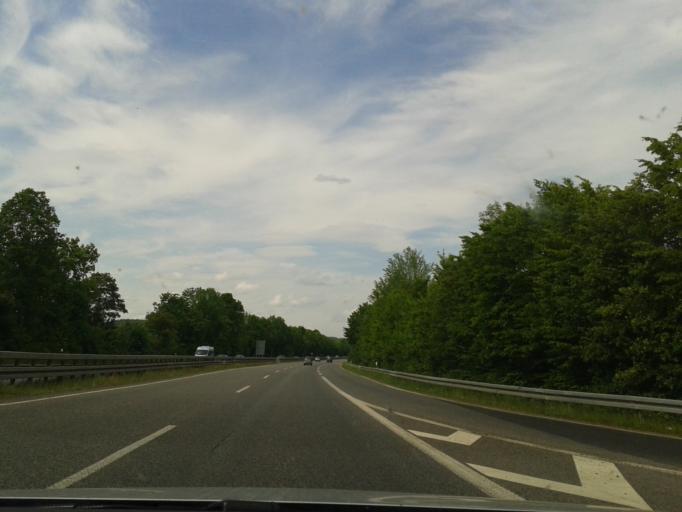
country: DE
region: Hesse
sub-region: Regierungsbezirk Giessen
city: Marburg an der Lahn
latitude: 50.8309
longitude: 8.7669
